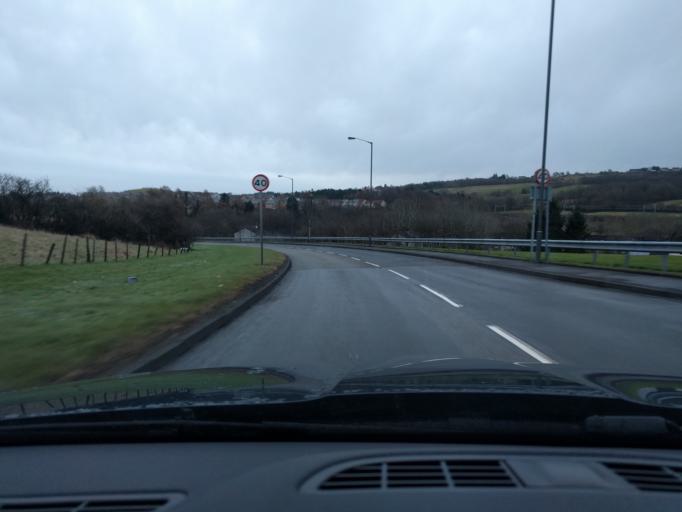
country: GB
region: Scotland
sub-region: Falkirk
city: Falkirk
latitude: 55.9865
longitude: -3.7647
